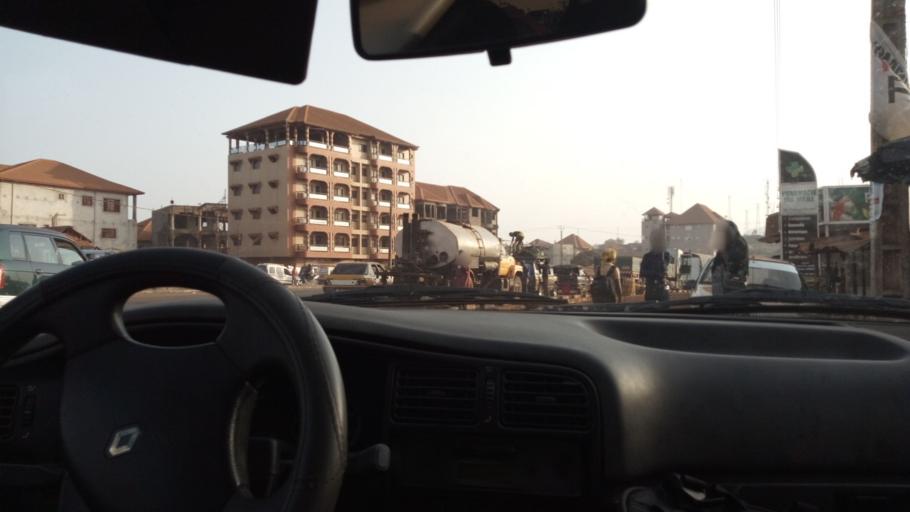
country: GN
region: Kindia
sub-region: Prefecture de Dubreka
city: Dubreka
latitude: 9.6771
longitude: -13.5434
